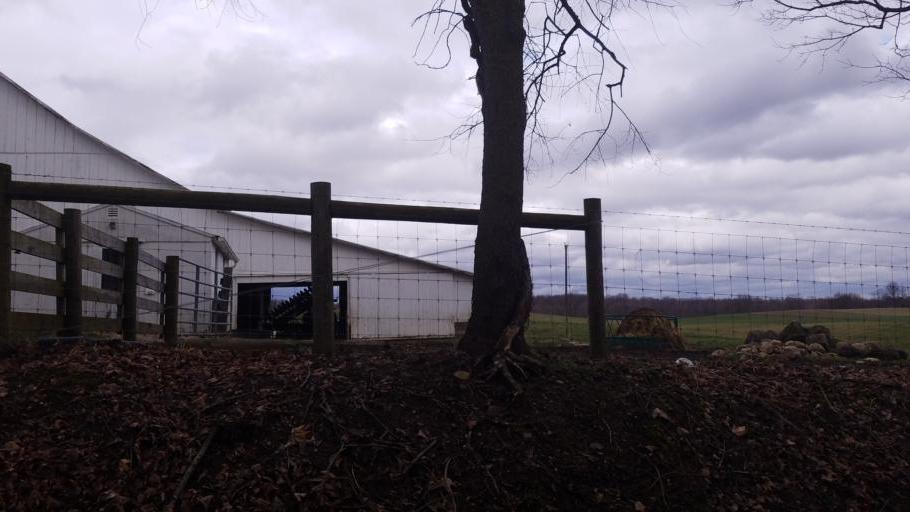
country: US
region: Ohio
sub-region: Knox County
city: Centerburg
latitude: 40.3367
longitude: -82.6070
